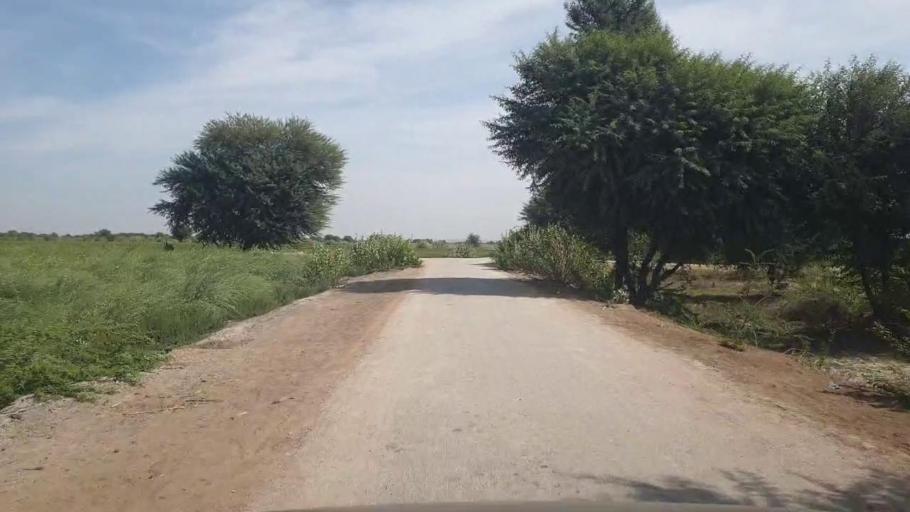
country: PK
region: Sindh
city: Kunri
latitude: 25.2144
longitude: 69.6376
